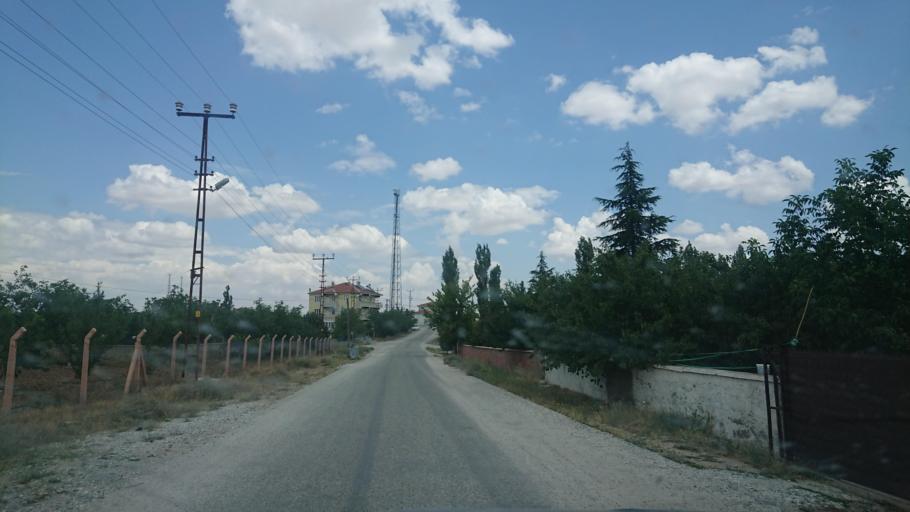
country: TR
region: Aksaray
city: Agacoren
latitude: 38.8750
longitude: 33.9109
